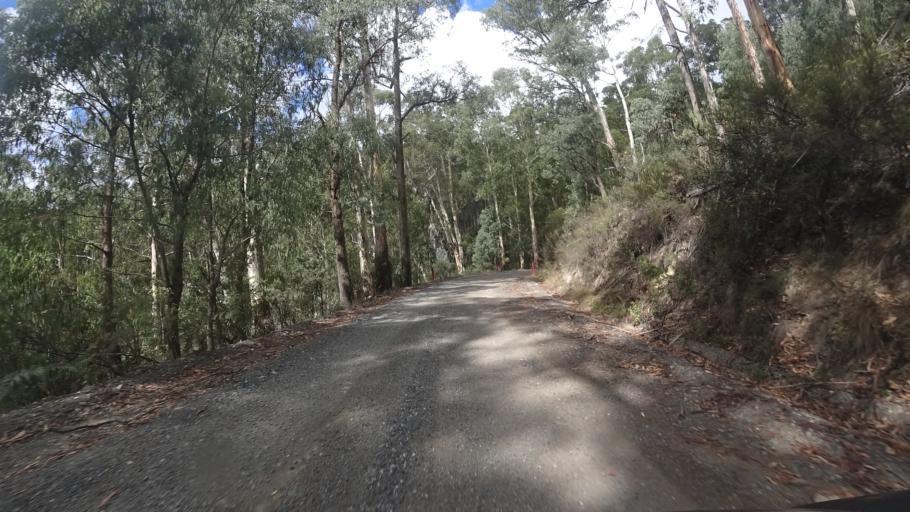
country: AU
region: New South Wales
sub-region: Tumut Shire
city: Tumut
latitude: -35.7299
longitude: 148.5000
